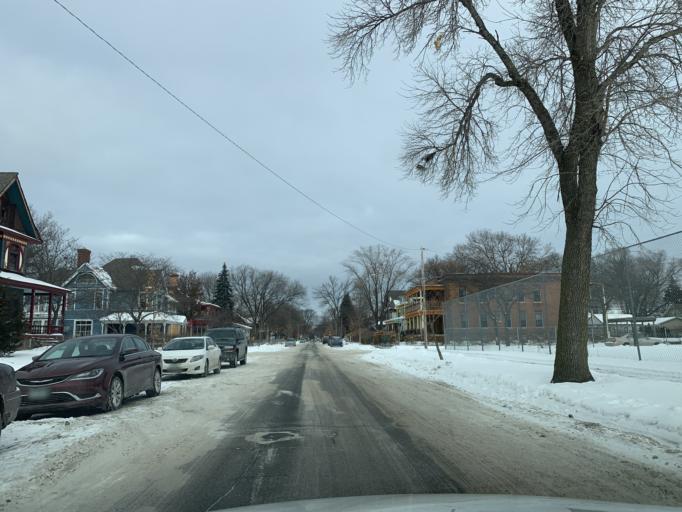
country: US
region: Minnesota
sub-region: Hennepin County
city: Minneapolis
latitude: 44.9938
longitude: -93.2921
